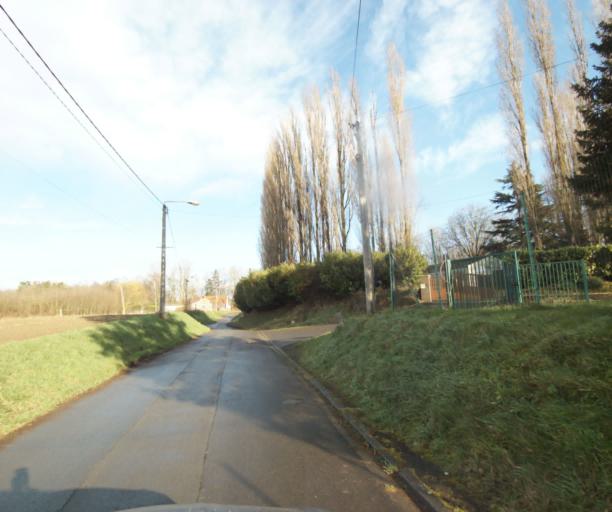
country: FR
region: Nord-Pas-de-Calais
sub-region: Departement du Nord
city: Saultain
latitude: 50.3468
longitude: 3.5711
